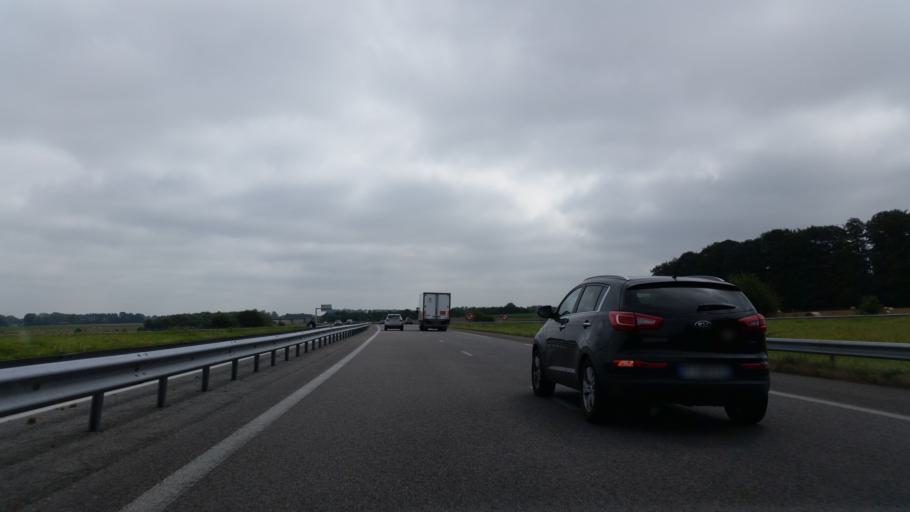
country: FR
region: Haute-Normandie
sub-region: Departement de la Seine-Maritime
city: Yerville
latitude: 49.6521
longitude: 0.8468
